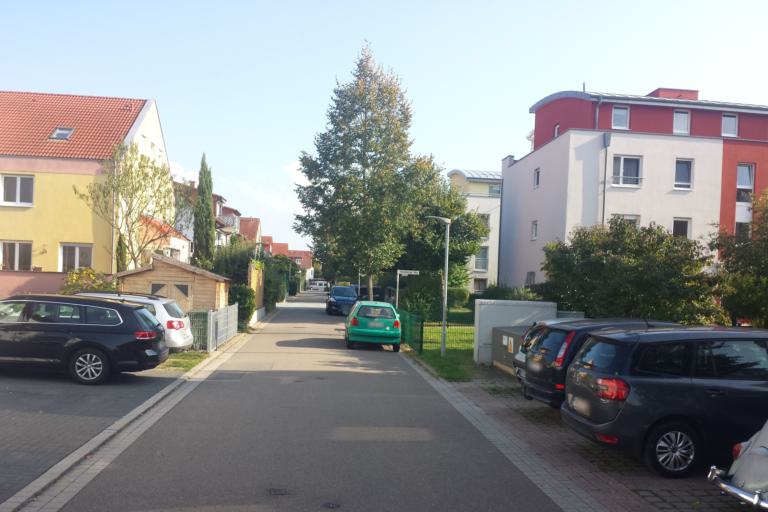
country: DE
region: Baden-Wuerttemberg
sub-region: Karlsruhe Region
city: Ilvesheim
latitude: 49.4759
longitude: 8.5699
